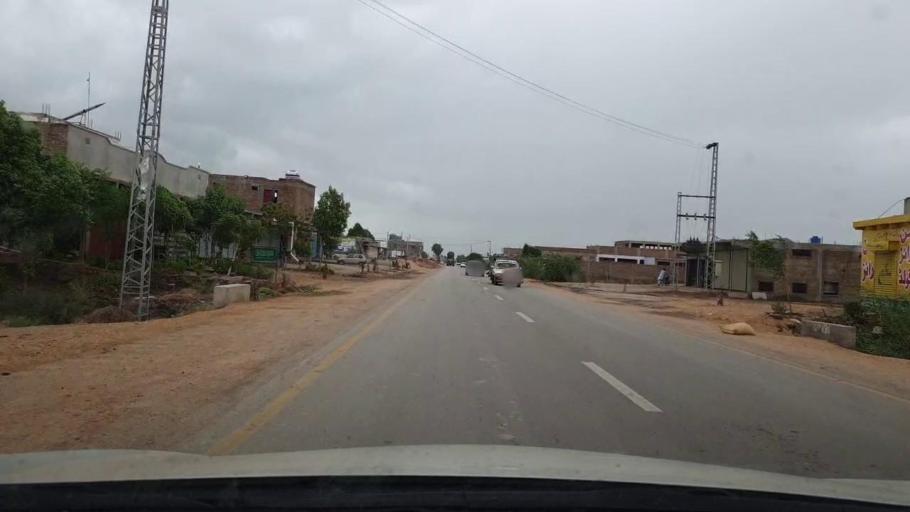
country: PK
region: Sindh
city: Kario
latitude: 24.6529
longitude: 68.5139
